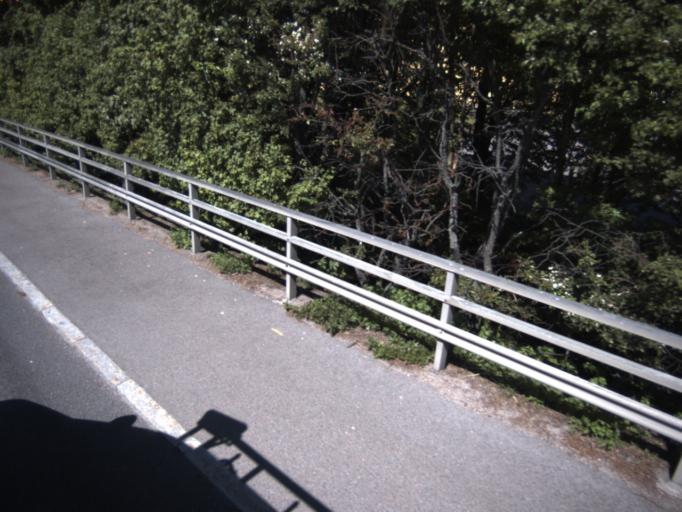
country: SE
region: Skane
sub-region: Helsingborg
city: Helsingborg
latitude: 56.0167
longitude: 12.7333
